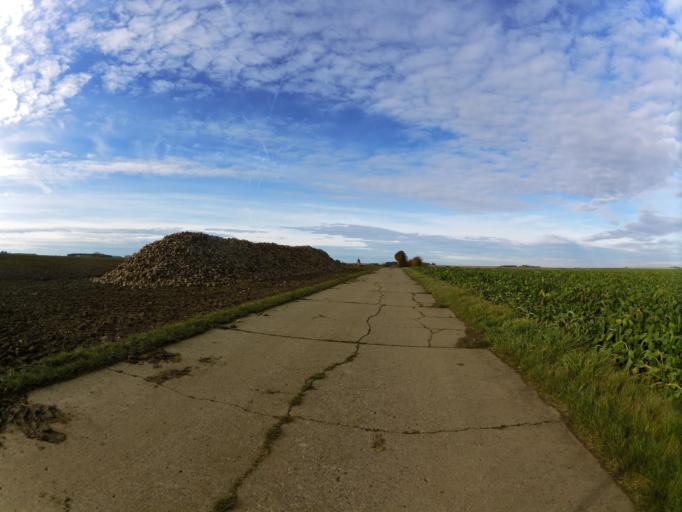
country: DE
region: Bavaria
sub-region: Regierungsbezirk Unterfranken
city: Giebelstadt
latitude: 49.6649
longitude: 9.9660
